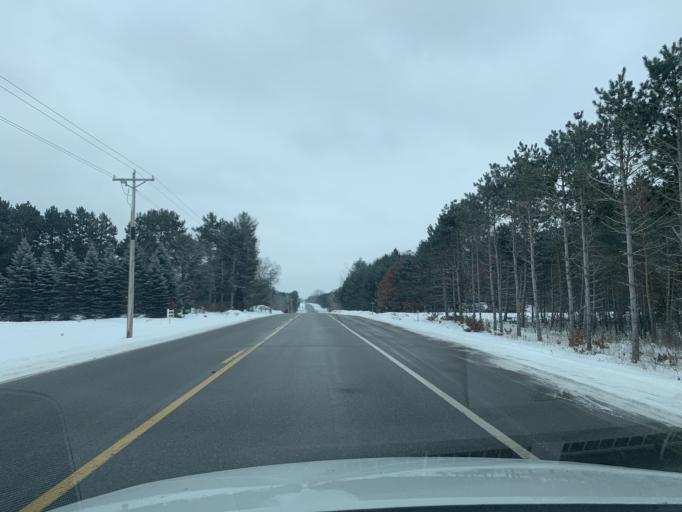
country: US
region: Minnesota
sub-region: Sherburne County
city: Zimmerman
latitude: 45.5013
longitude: -93.6198
